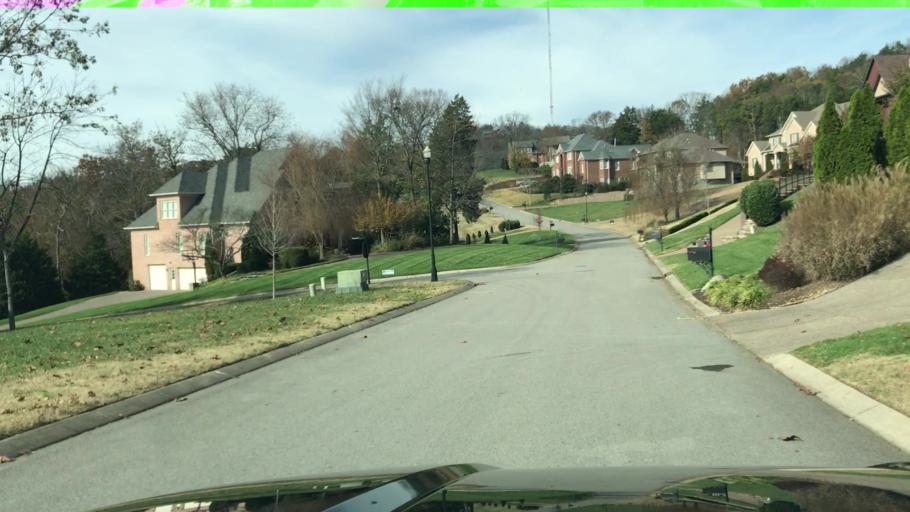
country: US
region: Tennessee
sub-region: Davidson County
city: Forest Hills
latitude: 36.0257
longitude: -86.8442
